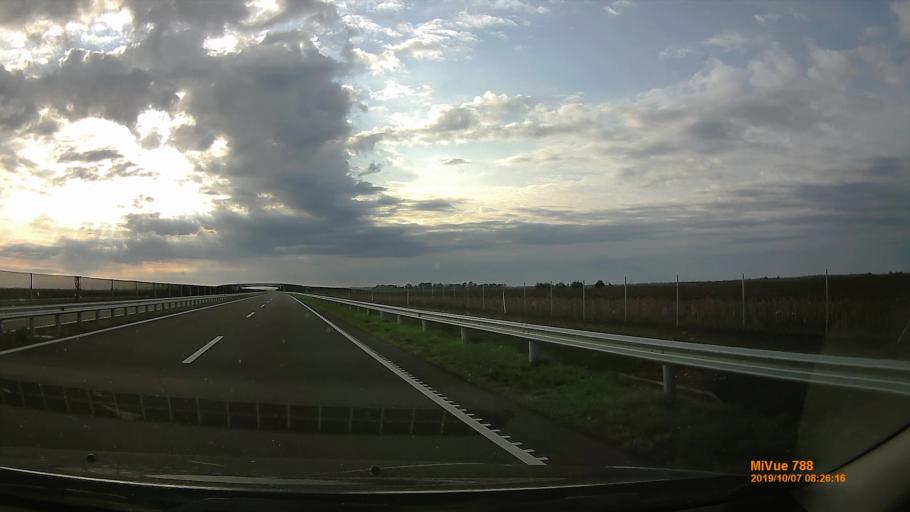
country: HU
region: Jasz-Nagykun-Szolnok
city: Kunszentmarton
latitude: 46.8229
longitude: 20.3673
